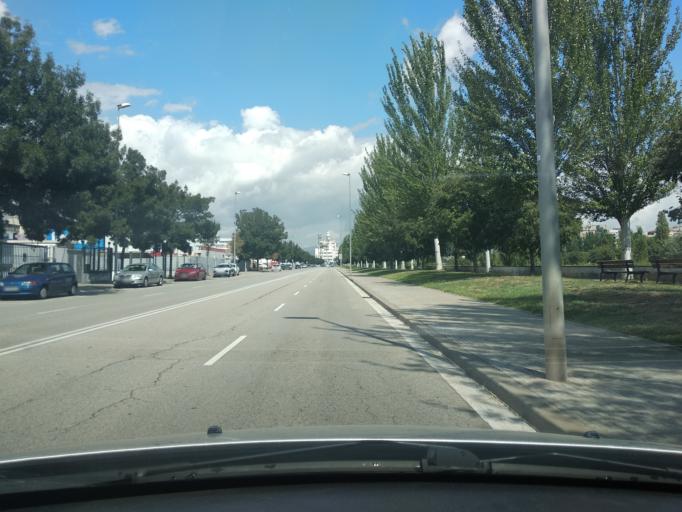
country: ES
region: Catalonia
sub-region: Provincia de Barcelona
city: Granollers
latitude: 41.6033
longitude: 2.2789
